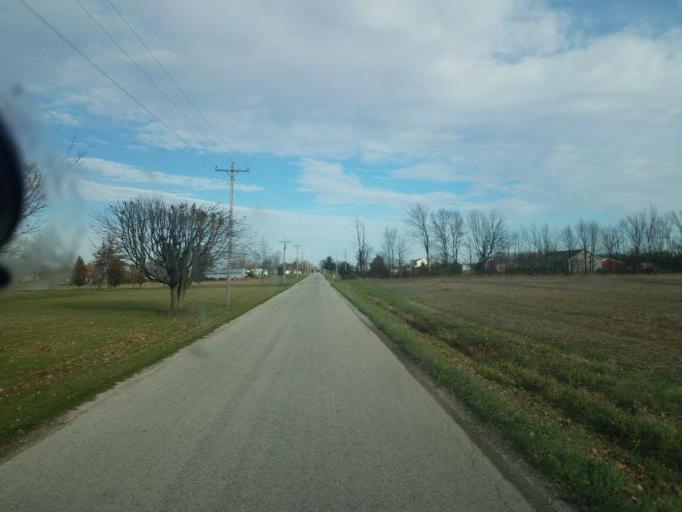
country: US
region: Ohio
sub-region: Crawford County
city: Bucyrus
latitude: 40.6681
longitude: -82.9483
